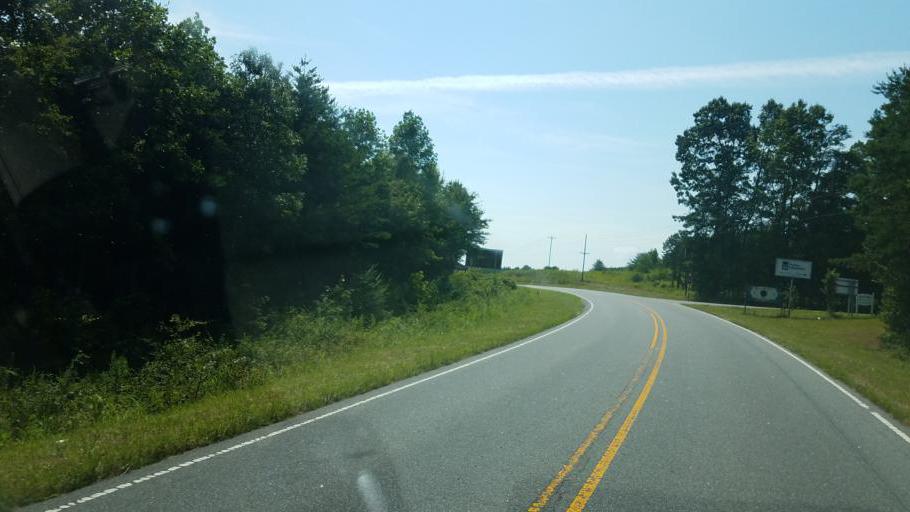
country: US
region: North Carolina
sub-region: Burke County
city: Icard
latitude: 35.5599
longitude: -81.5148
